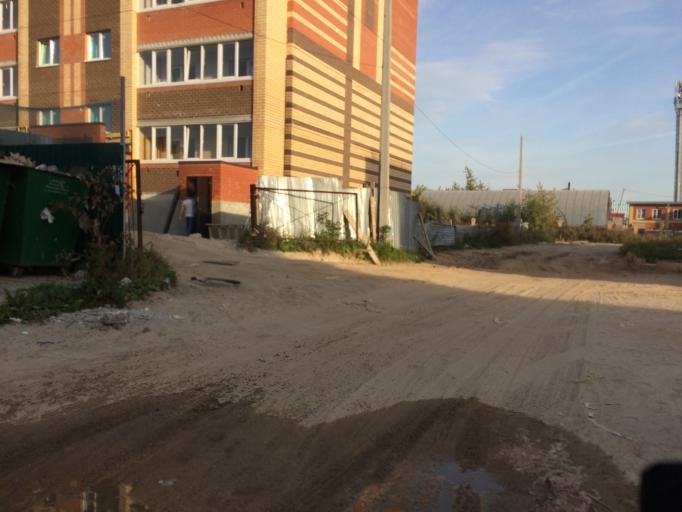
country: RU
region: Mariy-El
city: Yoshkar-Ola
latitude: 56.6271
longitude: 47.8500
